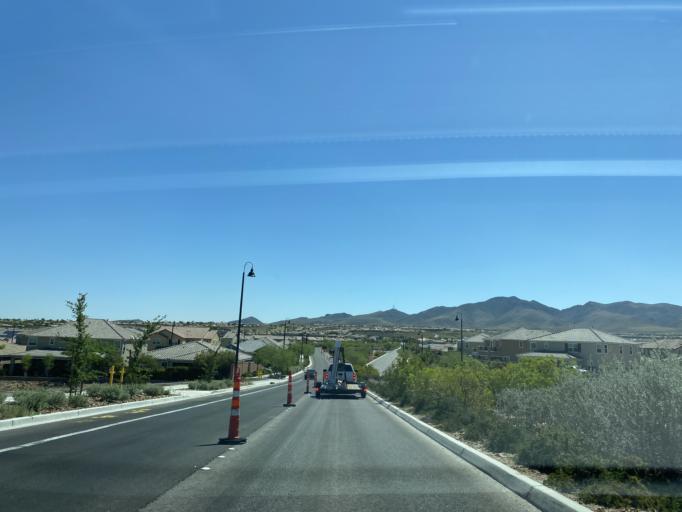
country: US
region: Nevada
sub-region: Clark County
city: Whitney
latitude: 35.9405
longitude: -115.1280
